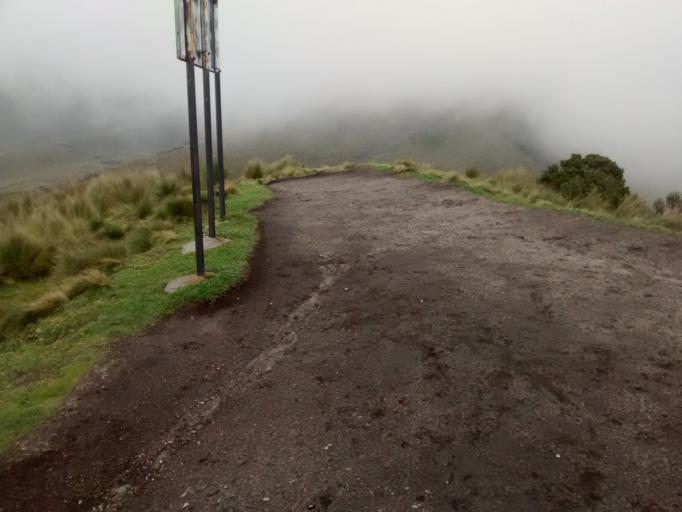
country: EC
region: Pichincha
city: Quito
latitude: -0.1822
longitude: -78.5383
